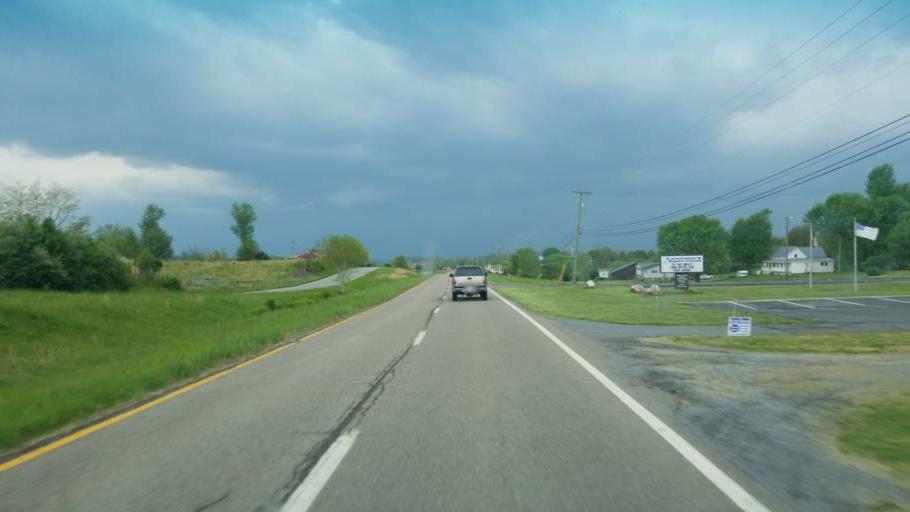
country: US
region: Virginia
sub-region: Washington County
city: Glade Spring
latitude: 36.7732
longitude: -81.7683
